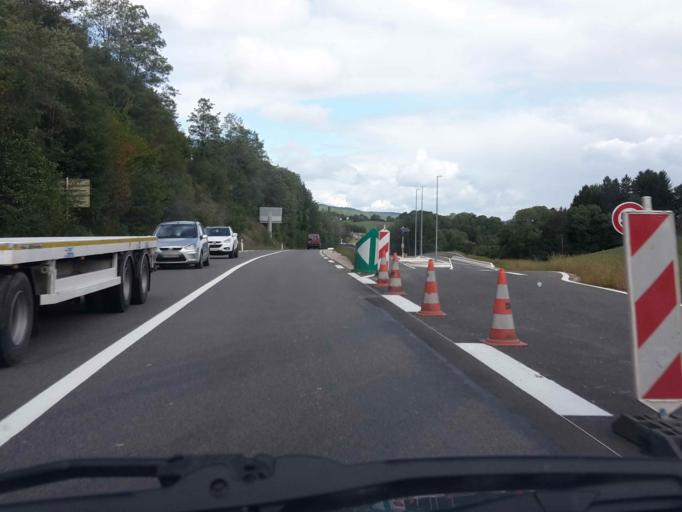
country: FR
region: Franche-Comte
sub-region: Departement du Doubs
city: Morre
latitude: 47.2182
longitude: 6.0681
